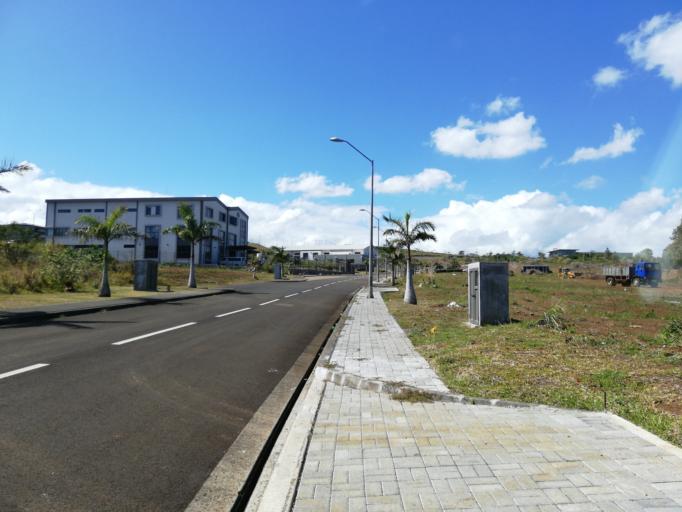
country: MU
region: Moka
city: Moka
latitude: -20.2228
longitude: 57.4886
